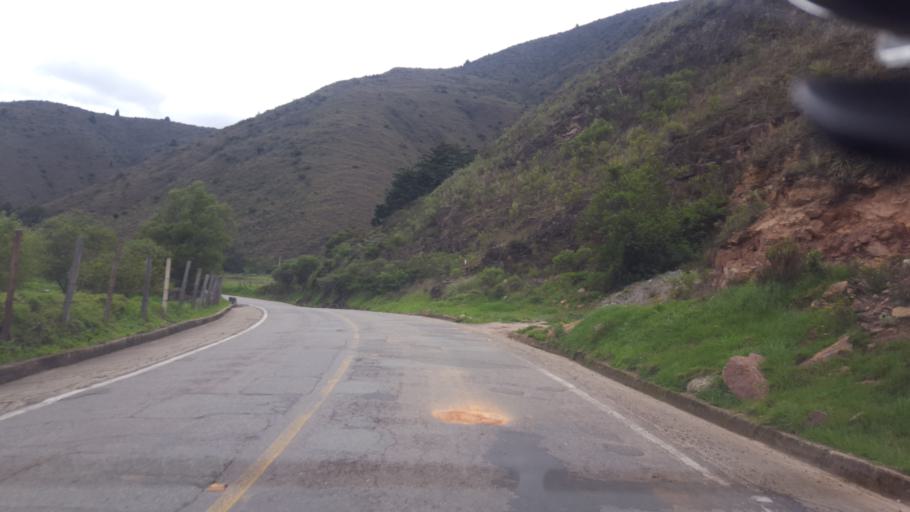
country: CO
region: Boyaca
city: Belen
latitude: 6.0116
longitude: -72.8256
